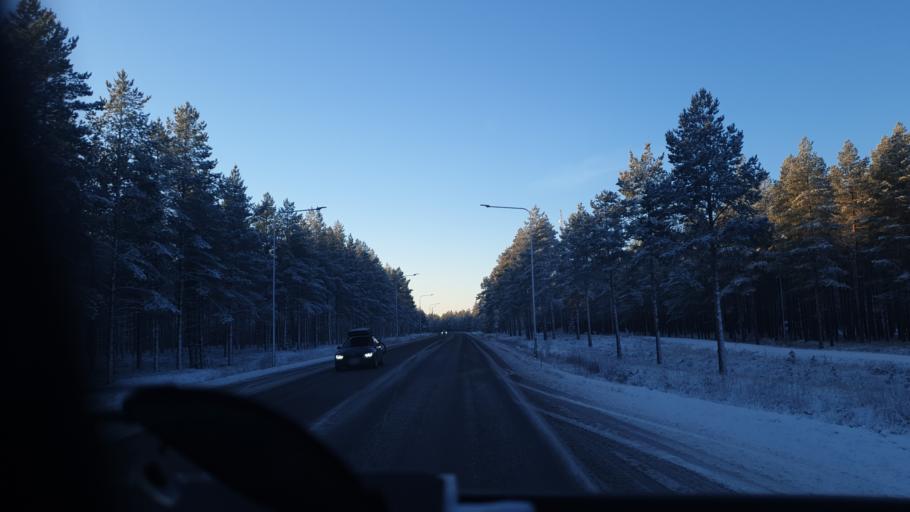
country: FI
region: Northern Ostrobothnia
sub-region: Ylivieska
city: Kalajoki
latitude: 64.2403
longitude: 23.8434
